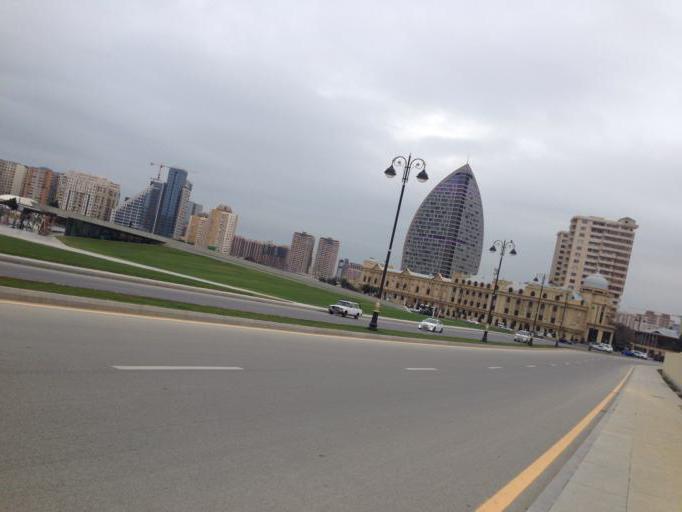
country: AZ
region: Baki
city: Baku
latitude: 40.3946
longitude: 49.8646
